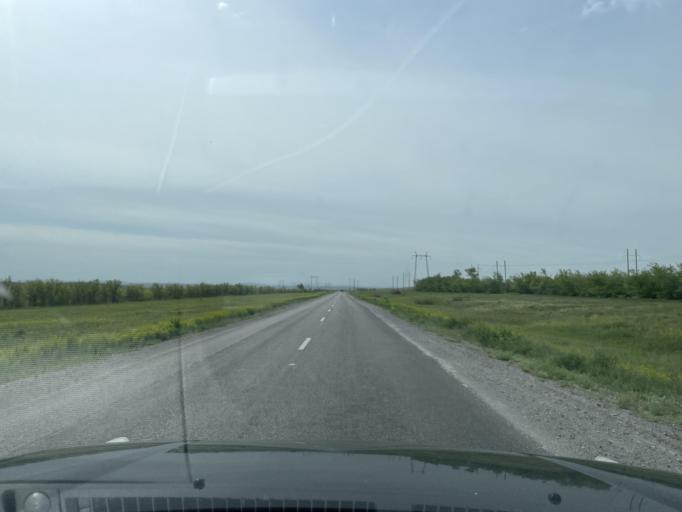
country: KZ
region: Qaraghandy
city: Abay
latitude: 49.4742
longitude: 72.9192
